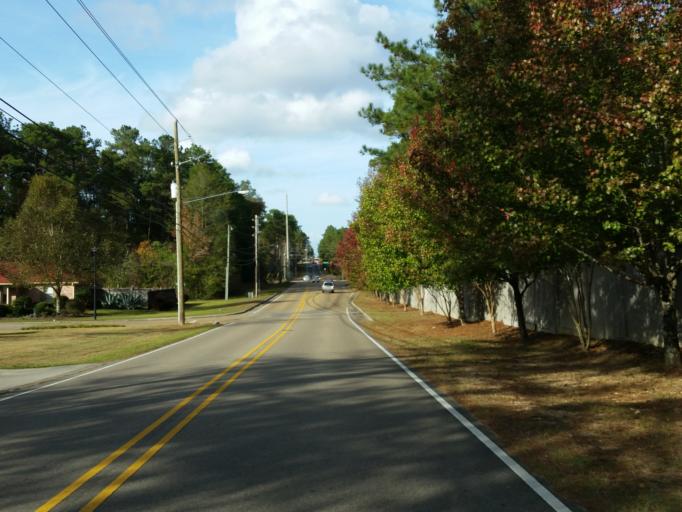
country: US
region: Mississippi
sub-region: Lamar County
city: West Hattiesburg
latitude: 31.3021
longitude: -89.3479
